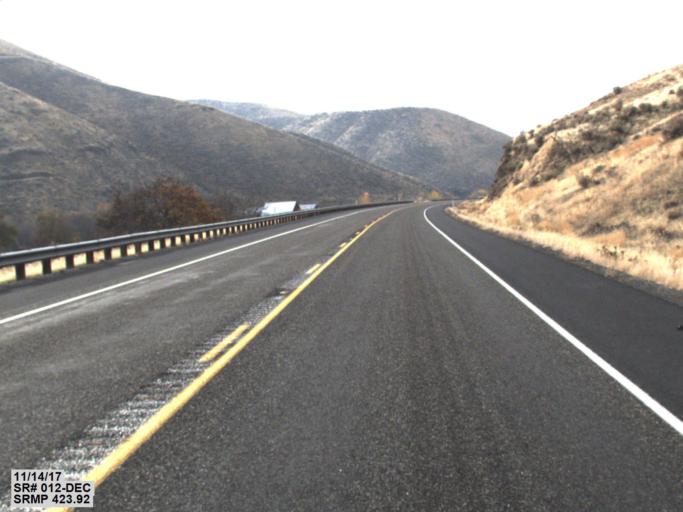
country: US
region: Washington
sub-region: Asotin County
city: Clarkston Heights-Vineland
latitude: 46.4042
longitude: -117.2326
